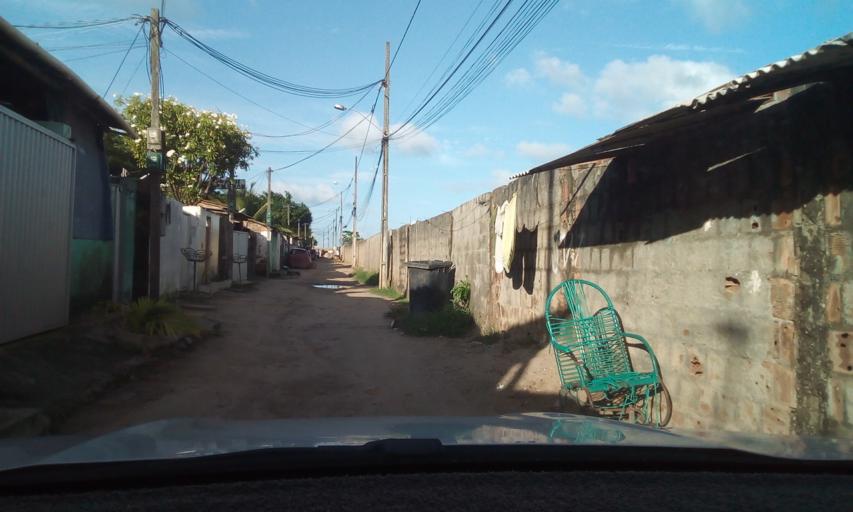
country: BR
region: Paraiba
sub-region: Joao Pessoa
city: Joao Pessoa
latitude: -7.1384
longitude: -34.8245
